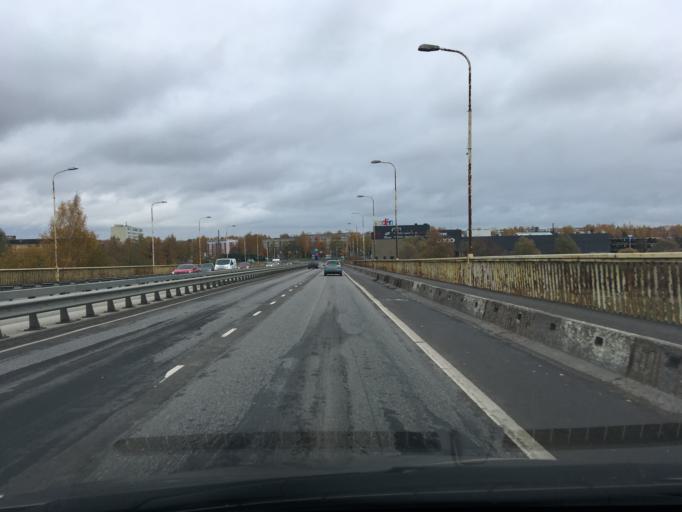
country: EE
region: Tartu
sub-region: Tartu linn
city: Tartu
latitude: 58.3713
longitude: 26.7438
